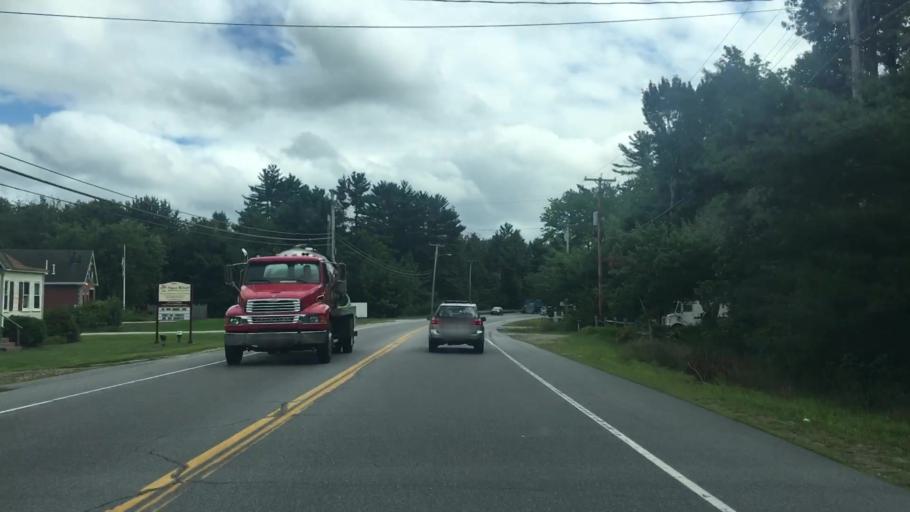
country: US
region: Maine
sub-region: York County
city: Waterboro
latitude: 43.5438
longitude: -70.7099
